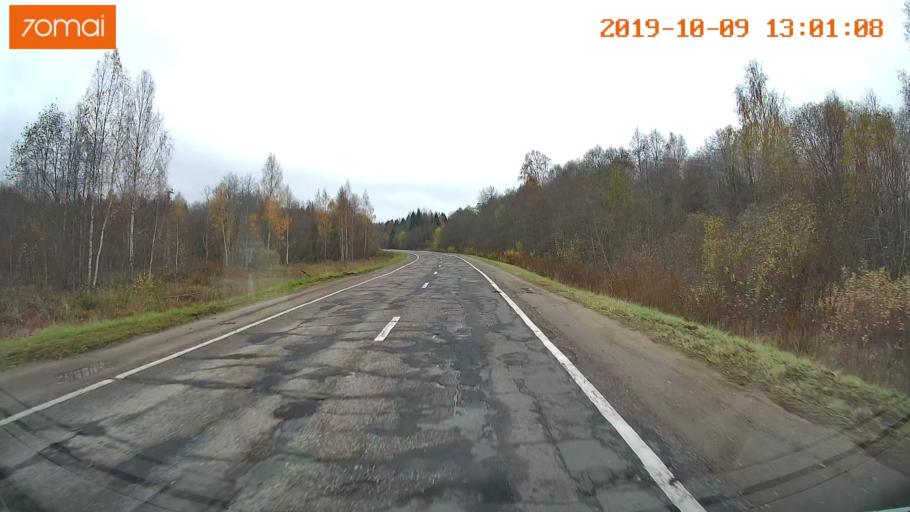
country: RU
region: Jaroslavl
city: Prechistoye
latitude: 58.3708
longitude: 40.4844
